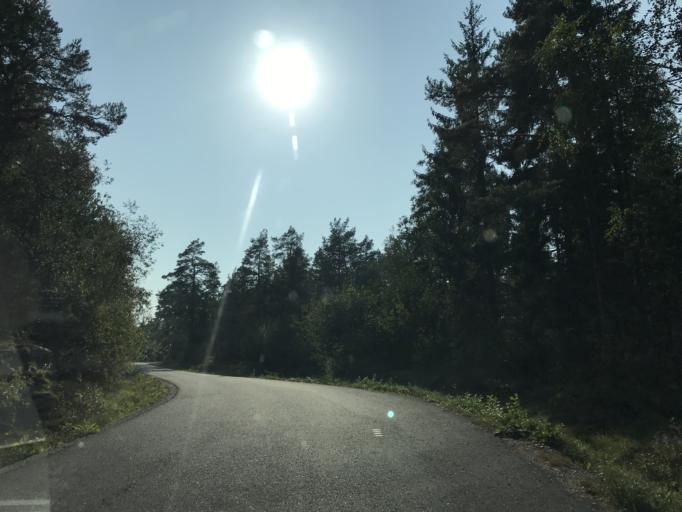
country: SE
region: Stockholm
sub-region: Norrtalje Kommun
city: Bjorko
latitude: 59.8607
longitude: 19.0322
